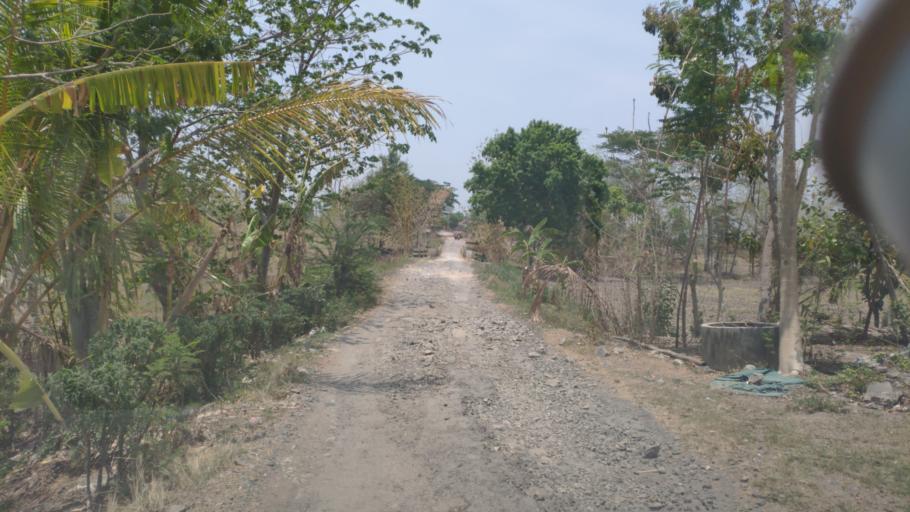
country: ID
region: Central Java
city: Randublatung
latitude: -7.1986
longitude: 111.2678
